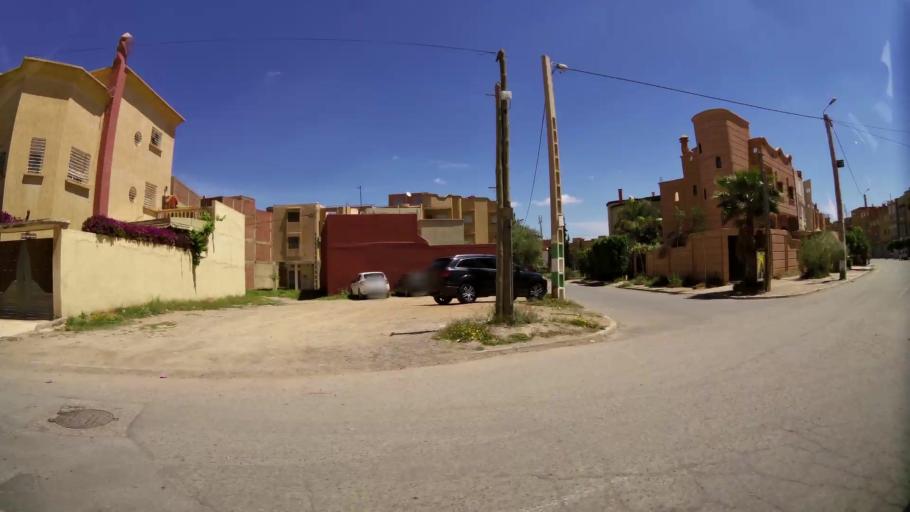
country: MA
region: Oriental
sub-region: Oujda-Angad
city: Oujda
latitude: 34.6627
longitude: -1.9434
